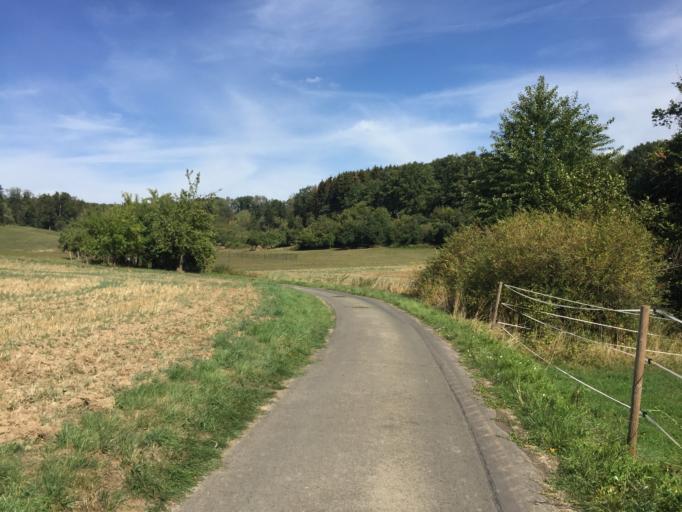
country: DE
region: Hesse
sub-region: Regierungsbezirk Giessen
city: Grunberg
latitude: 50.6033
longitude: 8.8976
